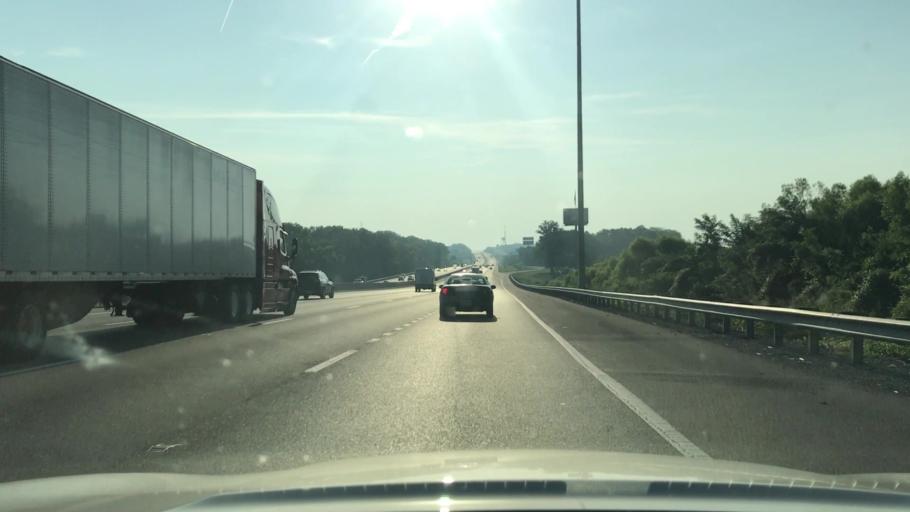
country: US
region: Tennessee
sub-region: Wilson County
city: Mount Juliet
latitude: 36.1719
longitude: -86.5077
